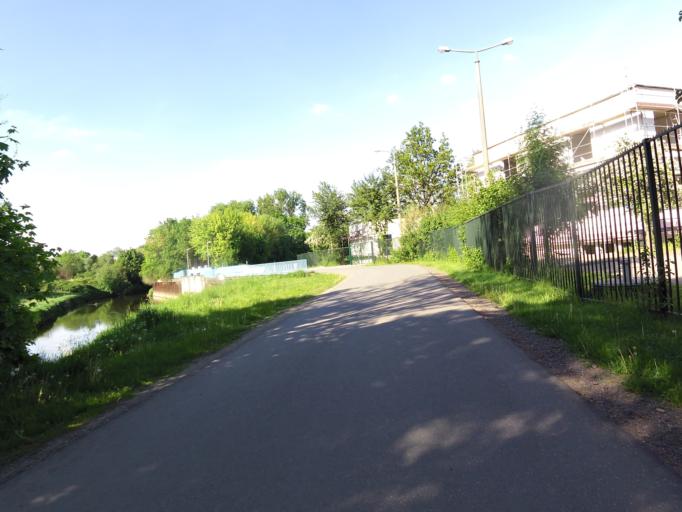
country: DE
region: Saxony
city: Markkleeberg
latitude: 51.3051
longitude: 12.3416
